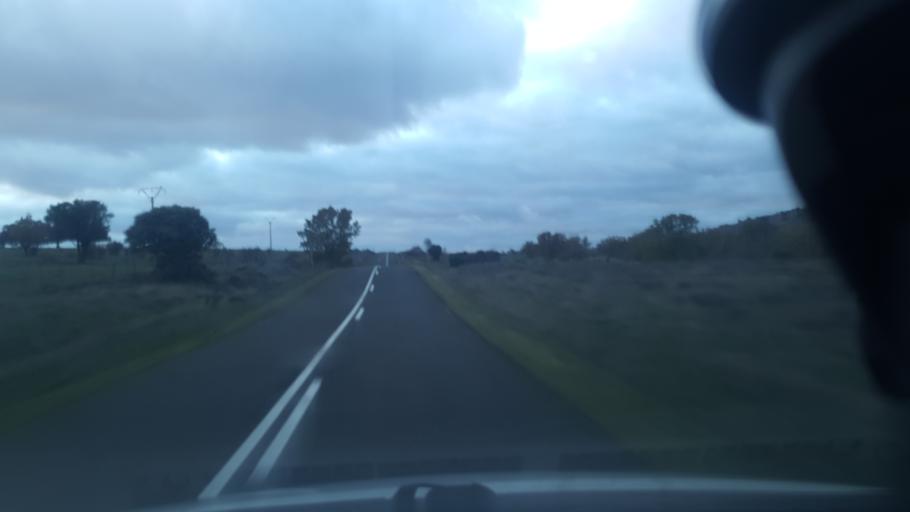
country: ES
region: Castille and Leon
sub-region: Provincia de Segovia
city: Villacastin
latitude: 40.7051
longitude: -4.3447
